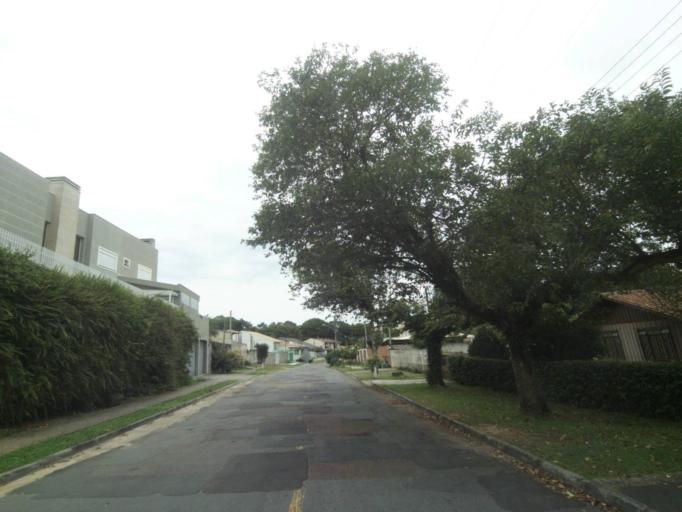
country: BR
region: Parana
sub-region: Curitiba
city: Curitiba
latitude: -25.4003
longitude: -49.2950
